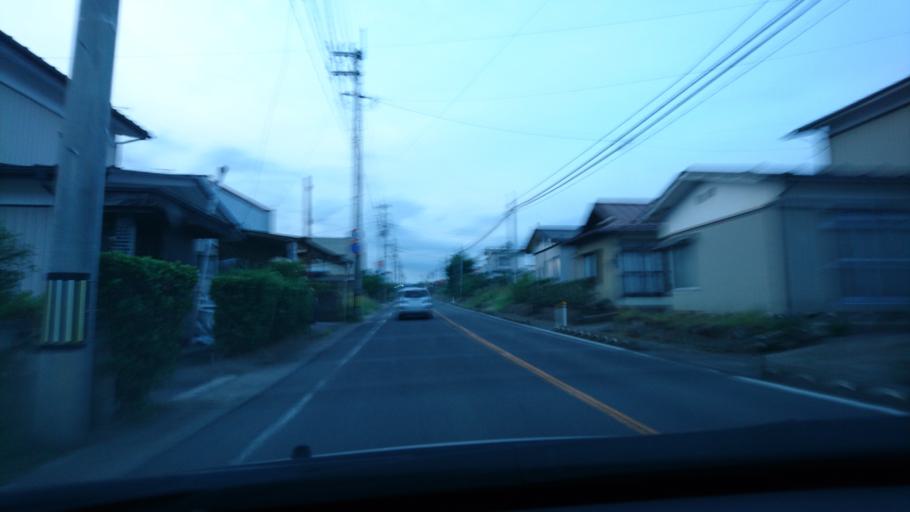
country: JP
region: Iwate
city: Ichinoseki
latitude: 38.8171
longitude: 140.9858
